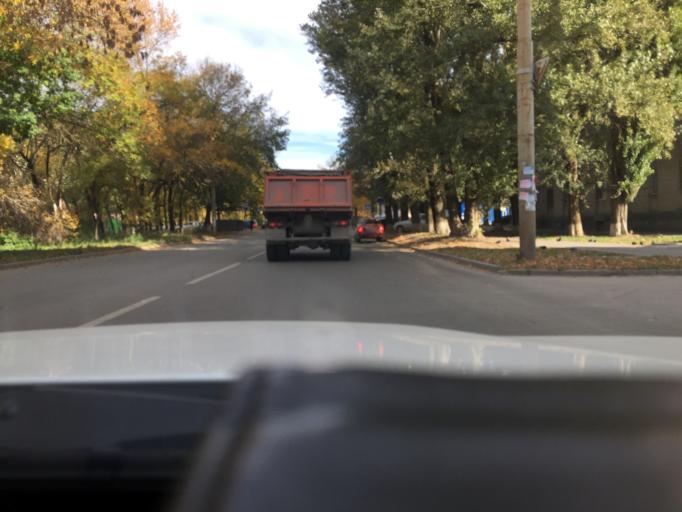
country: RU
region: Rostov
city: Imeni Chkalova
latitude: 47.2831
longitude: 39.8007
